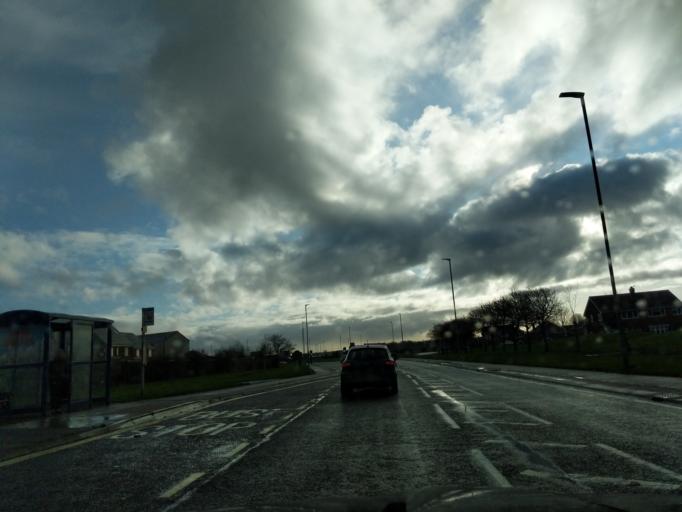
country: GB
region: England
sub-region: Northumberland
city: Blyth
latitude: 55.1110
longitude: -1.5044
